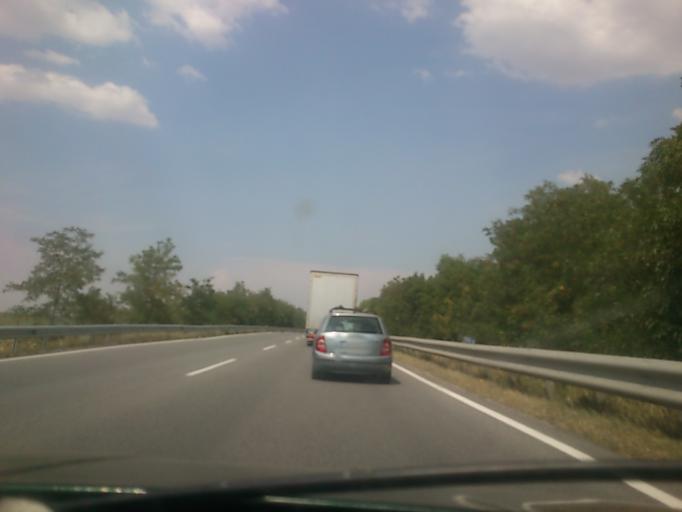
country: AT
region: Lower Austria
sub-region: Politischer Bezirk Mistelbach
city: Drasenhofen
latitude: 48.7306
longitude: 16.6573
